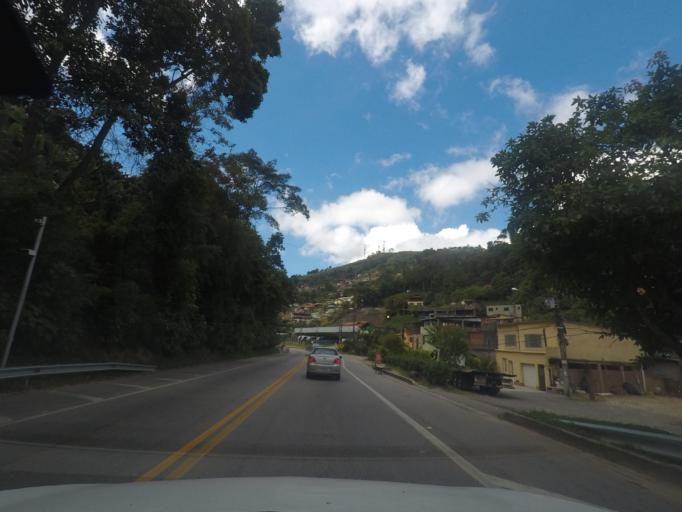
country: BR
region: Rio de Janeiro
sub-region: Teresopolis
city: Teresopolis
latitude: -22.3974
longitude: -42.9548
